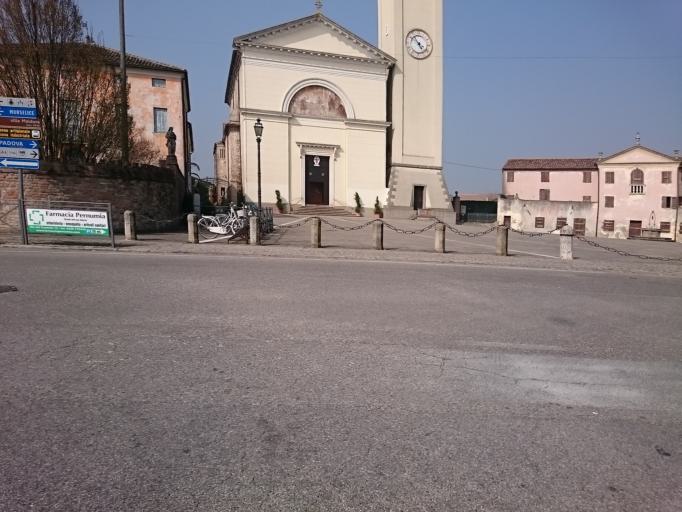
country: IT
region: Veneto
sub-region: Provincia di Padova
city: Pernumia
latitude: 45.2575
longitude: 11.7882
